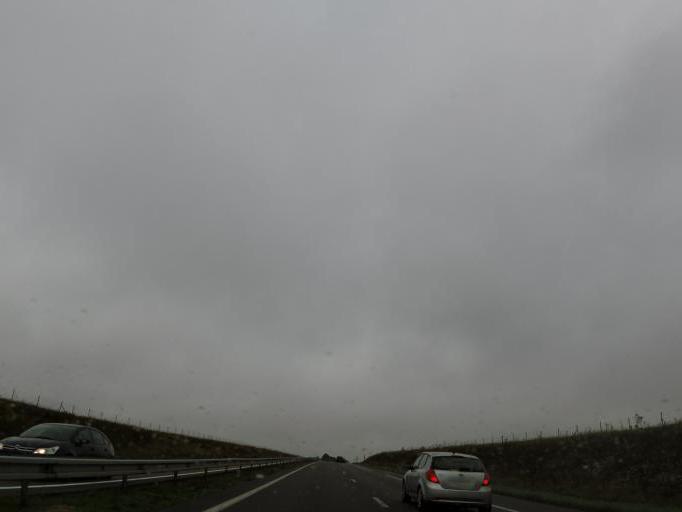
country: FR
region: Champagne-Ardenne
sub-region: Departement de la Marne
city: Verzy
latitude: 49.0905
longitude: 4.2583
